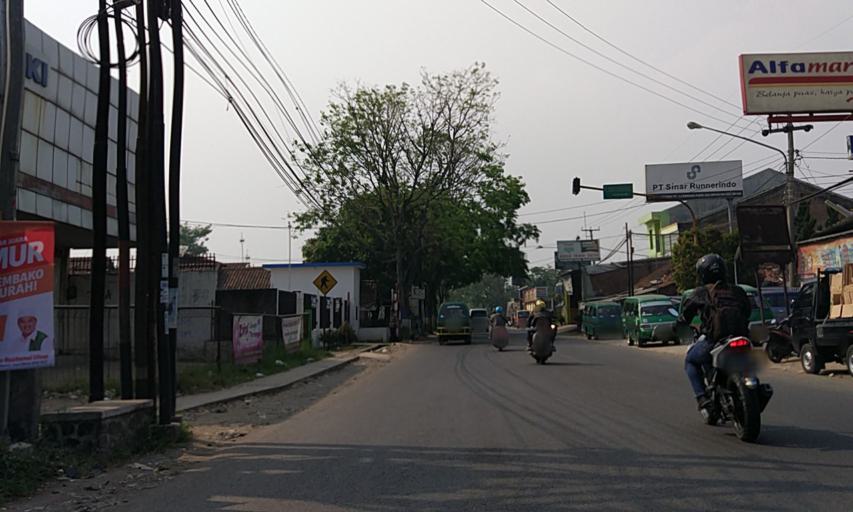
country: ID
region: West Java
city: Margahayukencana
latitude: -7.0031
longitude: 107.5525
